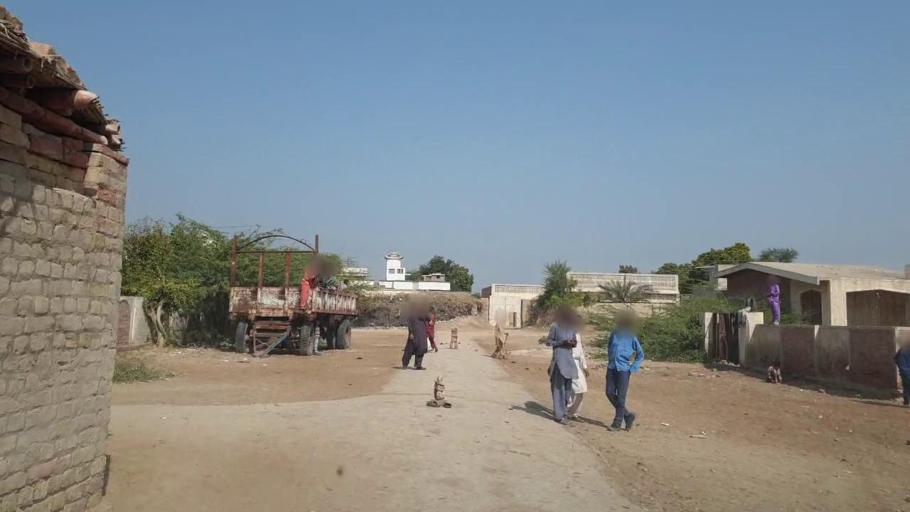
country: PK
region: Sindh
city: Mirpur Khas
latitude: 25.6232
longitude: 69.0913
